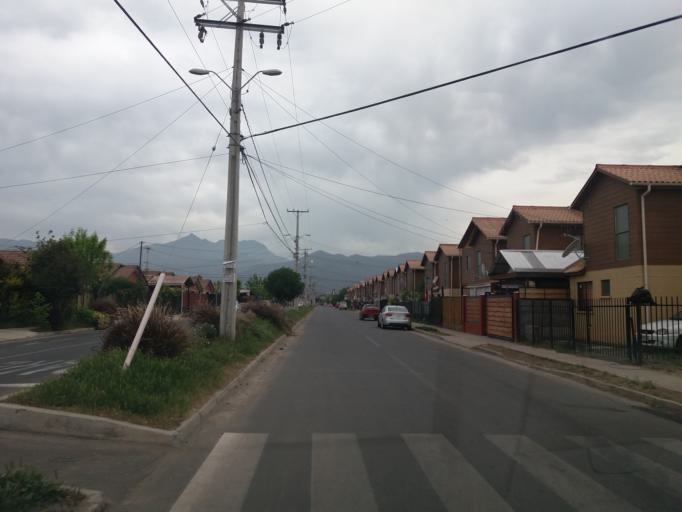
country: CL
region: Valparaiso
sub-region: Provincia de Quillota
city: Quillota
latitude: -32.8942
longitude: -71.2693
